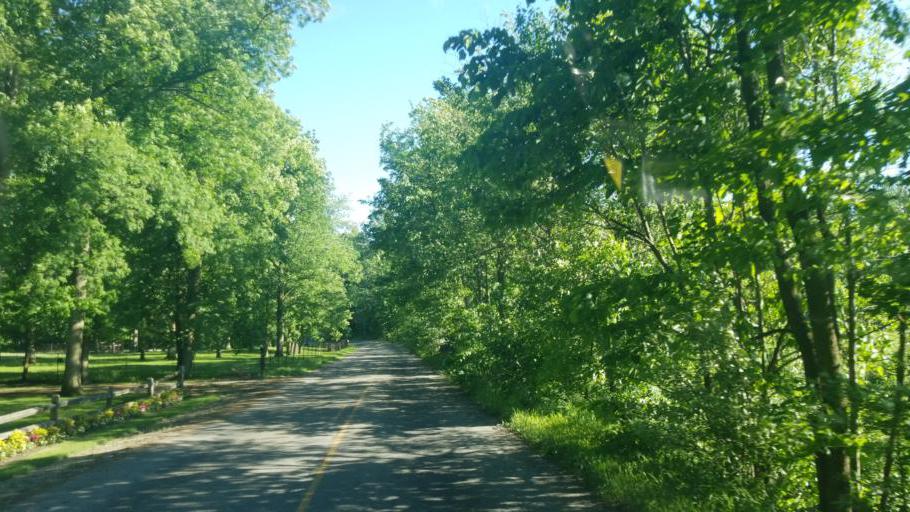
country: US
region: Indiana
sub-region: Elkhart County
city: Nappanee
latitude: 41.4367
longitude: -86.0496
